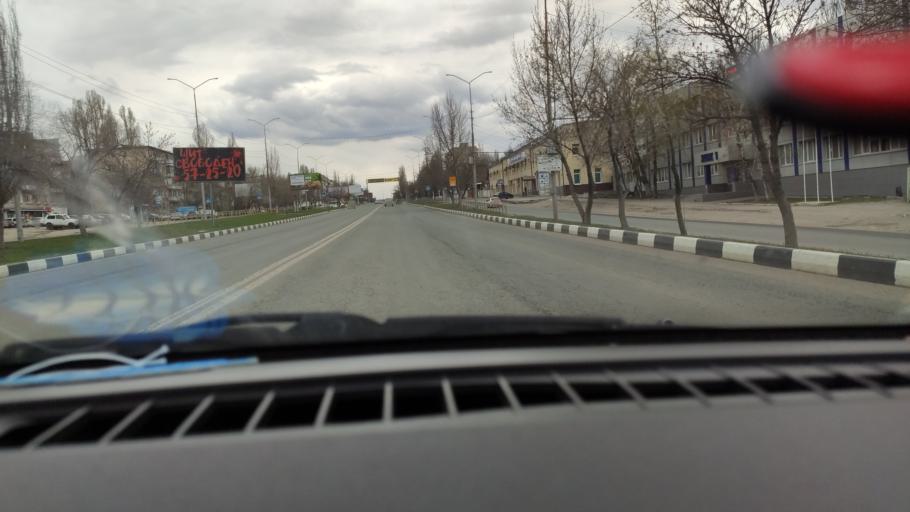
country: RU
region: Saratov
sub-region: Saratovskiy Rayon
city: Saratov
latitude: 51.6017
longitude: 45.9686
